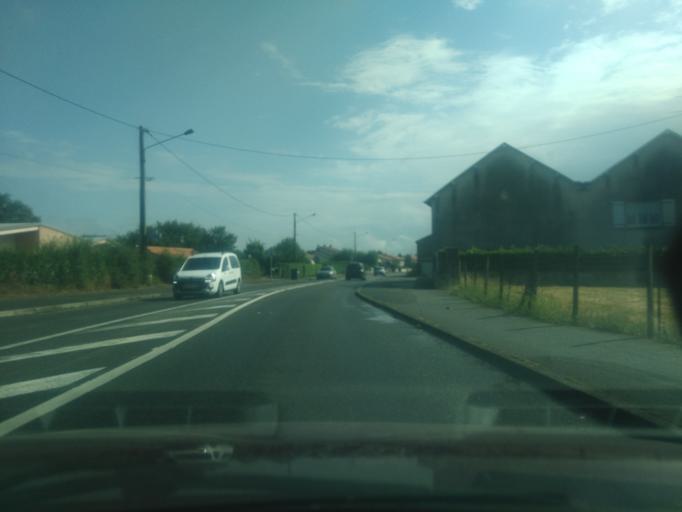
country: FR
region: Poitou-Charentes
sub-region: Departement des Deux-Sevres
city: Parthenay
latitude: 46.6388
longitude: -0.2413
